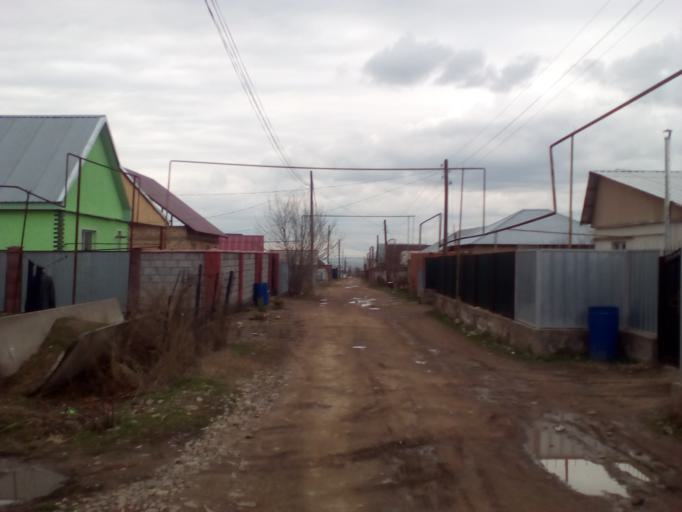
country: KZ
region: Almaty Oblysy
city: Burunday
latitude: 43.1809
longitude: 76.3964
